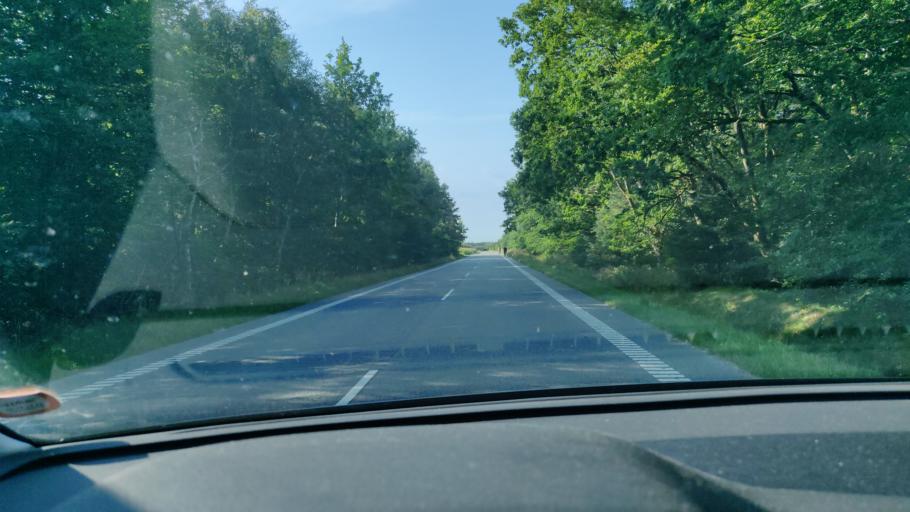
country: DK
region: North Denmark
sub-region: Jammerbugt Kommune
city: Pandrup
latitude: 57.2510
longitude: 9.6458
